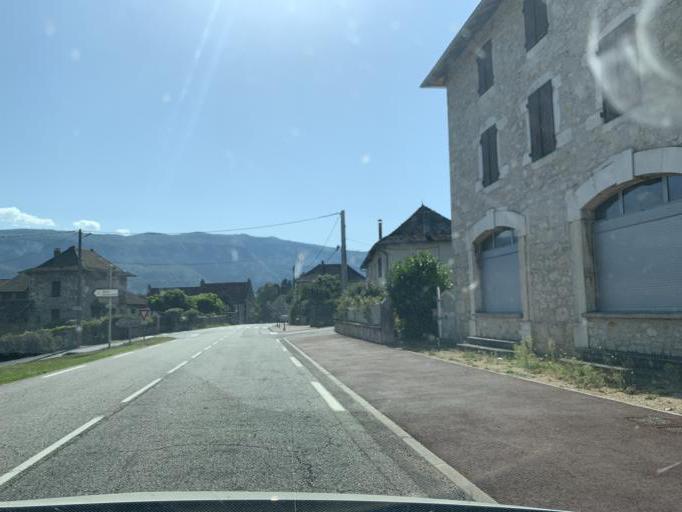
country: FR
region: Rhone-Alpes
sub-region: Departement de la Savoie
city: Yenne
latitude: 45.6764
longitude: 5.6773
